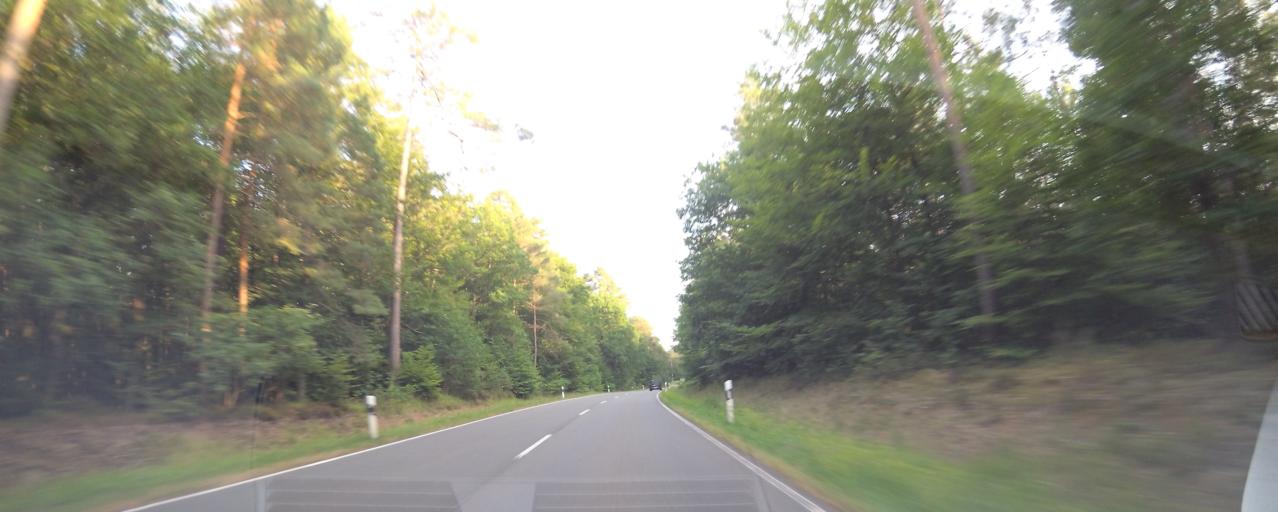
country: DE
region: Rheinland-Pfalz
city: Herforst
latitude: 49.9364
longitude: 6.6992
